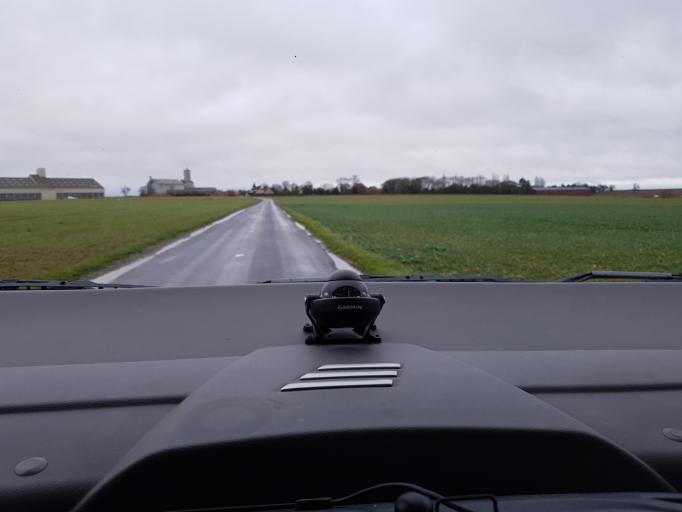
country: FR
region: Haute-Normandie
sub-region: Departement de l'Eure
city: Fleury-sur-Andelle
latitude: 49.2951
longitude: 1.3440
